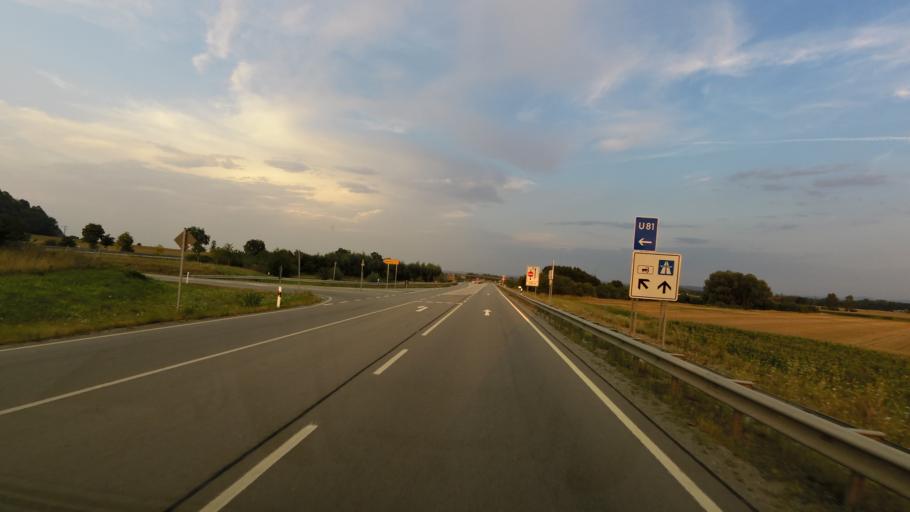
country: DE
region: Bavaria
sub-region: Lower Bavaria
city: Ering
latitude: 48.3078
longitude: 13.1679
